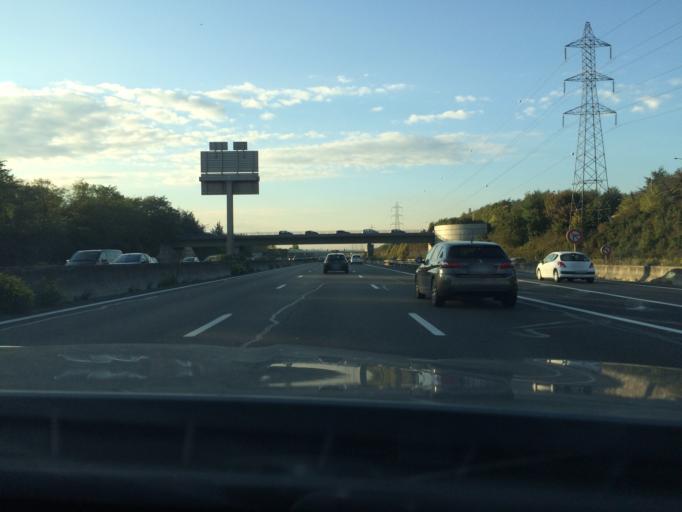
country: FR
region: Ile-de-France
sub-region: Departement de l'Essonne
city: Courcouronnes
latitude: 48.6231
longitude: 2.4212
